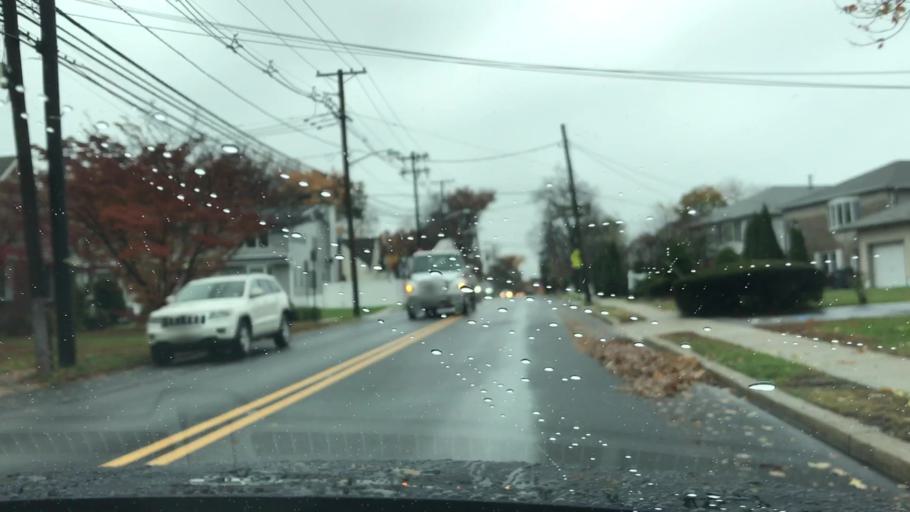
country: US
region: New Jersey
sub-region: Bergen County
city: Bergenfield
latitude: 40.9211
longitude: -74.0076
